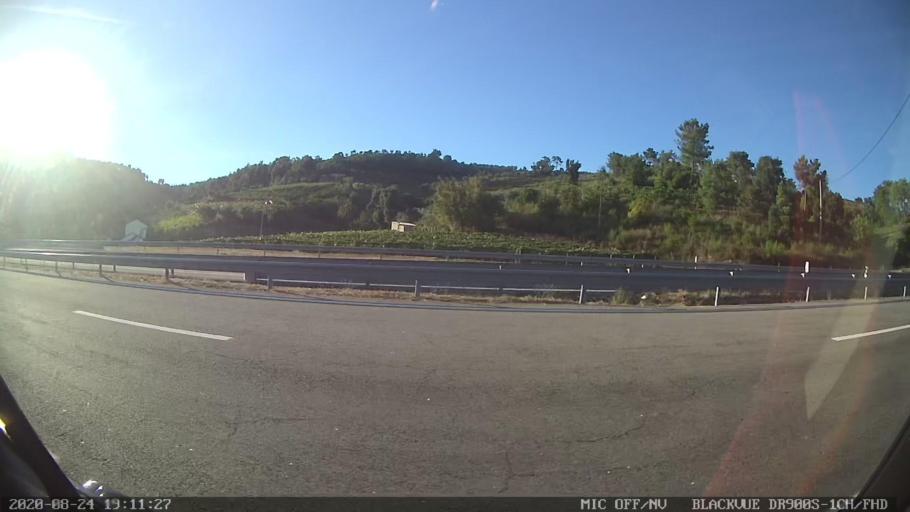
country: PT
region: Vila Real
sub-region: Santa Marta de Penaguiao
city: Santa Marta de Penaguiao
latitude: 41.2090
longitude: -7.7410
